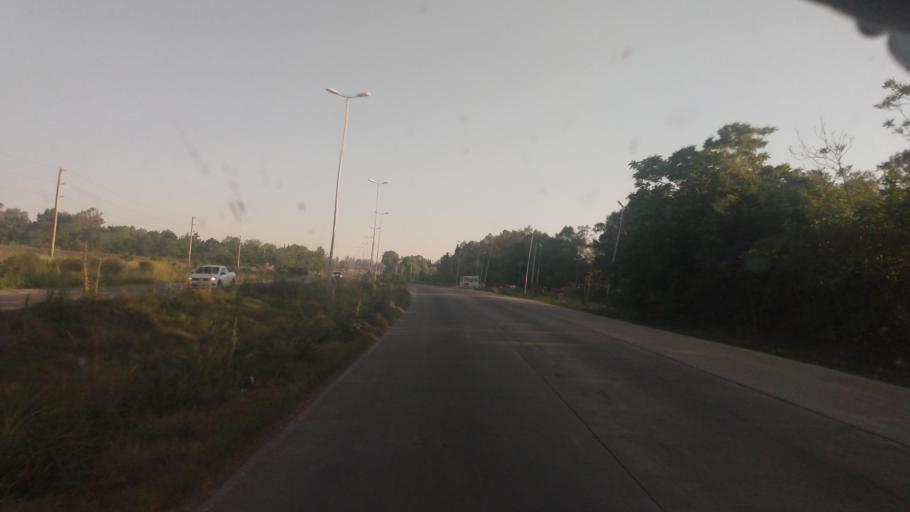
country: AR
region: Buenos Aires
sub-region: Partido de Campana
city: Campana
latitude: -34.2452
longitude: -58.9662
